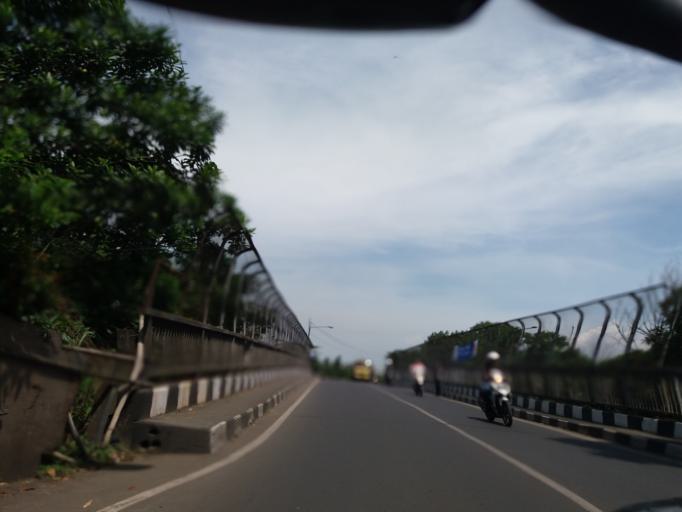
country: ID
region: West Java
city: Margahayukencana
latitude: -6.9310
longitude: 107.5727
